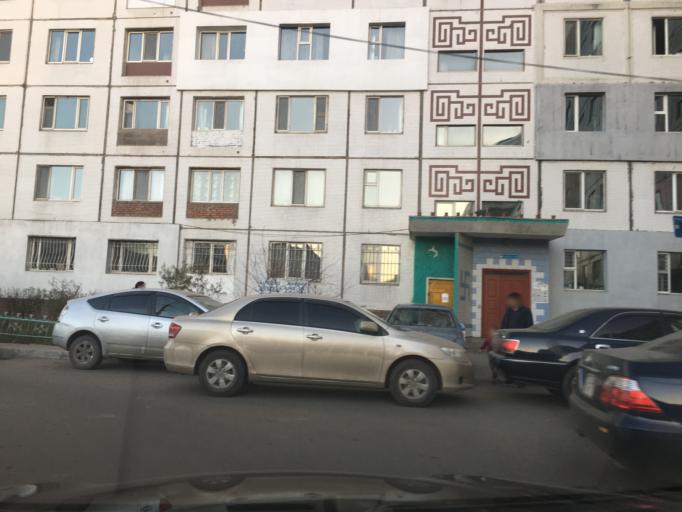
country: MN
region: Ulaanbaatar
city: Ulaanbaatar
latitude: 47.9238
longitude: 106.8872
